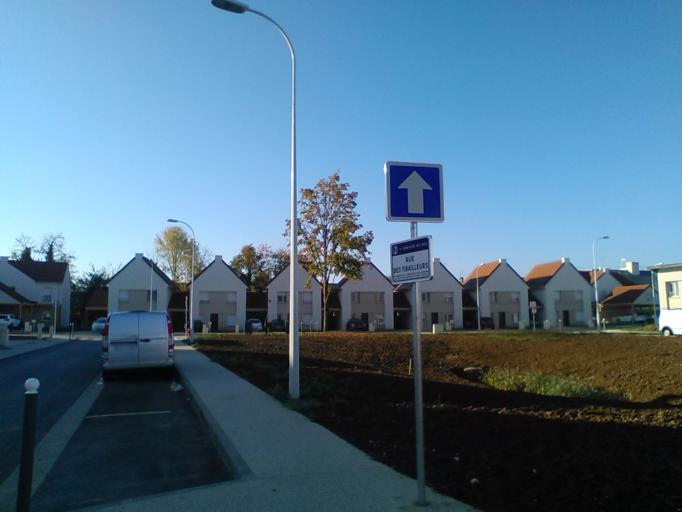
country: FR
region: Ile-de-France
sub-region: Departement de l'Essonne
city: Fleury-Merogis
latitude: 48.6308
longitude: 2.3419
